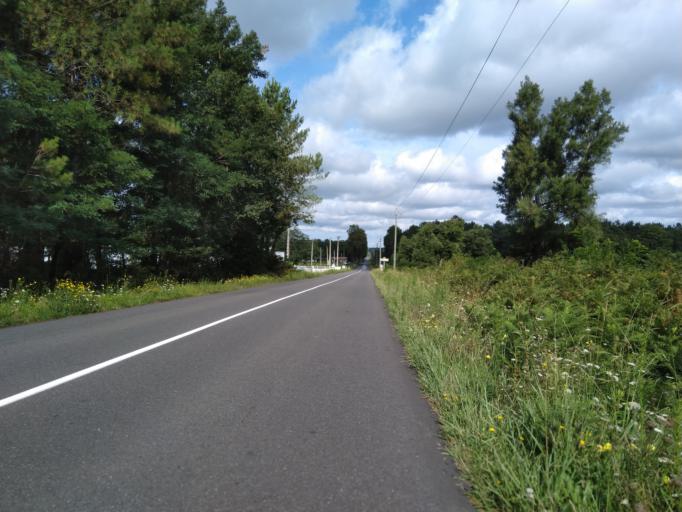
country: FR
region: Aquitaine
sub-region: Departement des Landes
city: Mees
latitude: 43.7338
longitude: -1.1063
